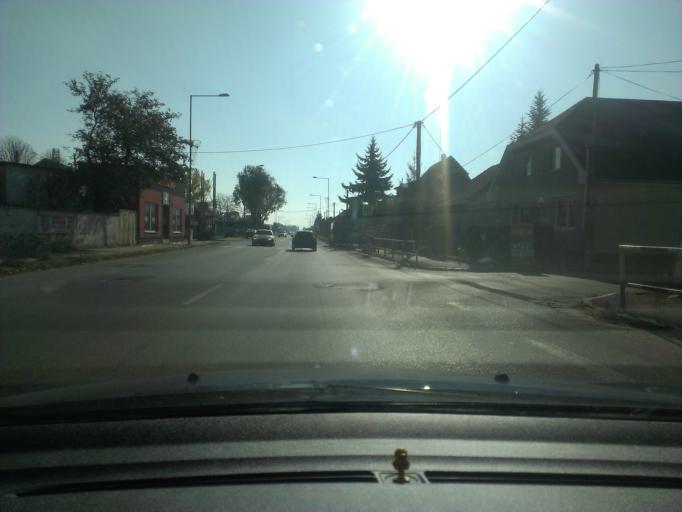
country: SK
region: Nitriansky
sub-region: Okres Nove Zamky
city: Nove Zamky
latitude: 47.9803
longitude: 18.1769
